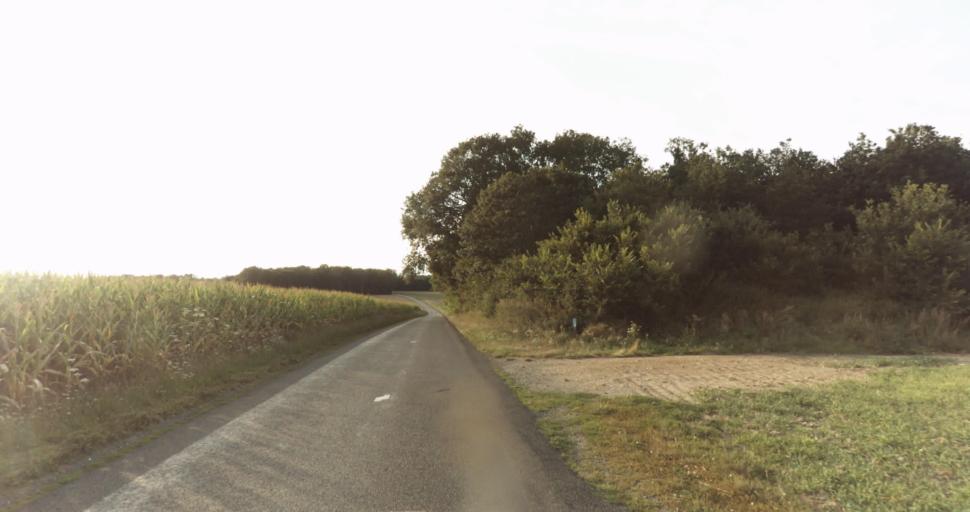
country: FR
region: Haute-Normandie
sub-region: Departement de l'Eure
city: Marcilly-sur-Eure
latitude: 48.8047
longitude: 1.3101
